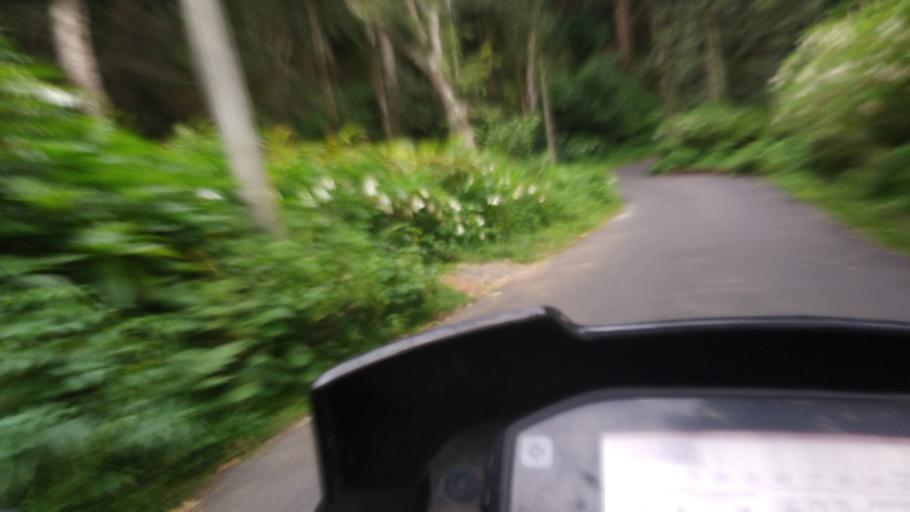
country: IN
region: Tamil Nadu
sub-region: Theni
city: Bodinayakkanur
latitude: 10.0344
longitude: 77.2303
